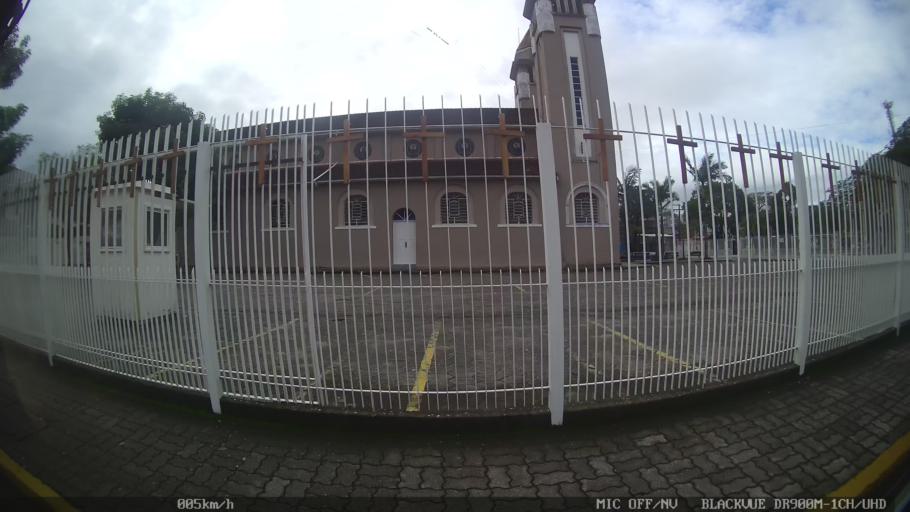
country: BR
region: Santa Catarina
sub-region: Biguacu
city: Biguacu
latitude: -27.4952
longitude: -48.6556
